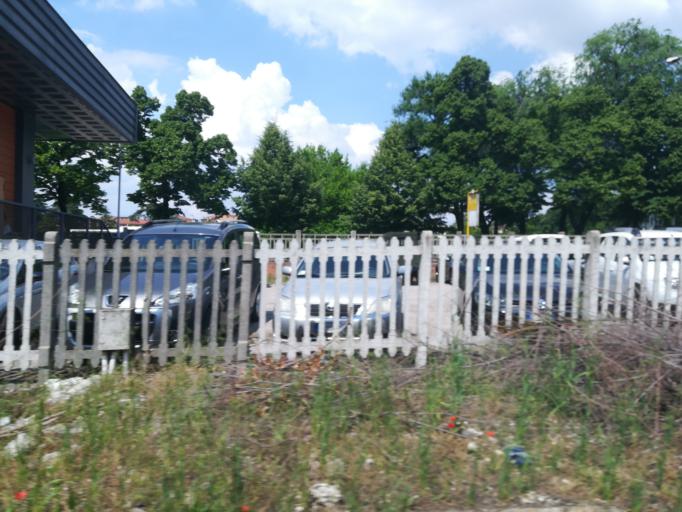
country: IT
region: Veneto
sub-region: Provincia di Vicenza
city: Vicenza
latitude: 45.5408
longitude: 11.5443
